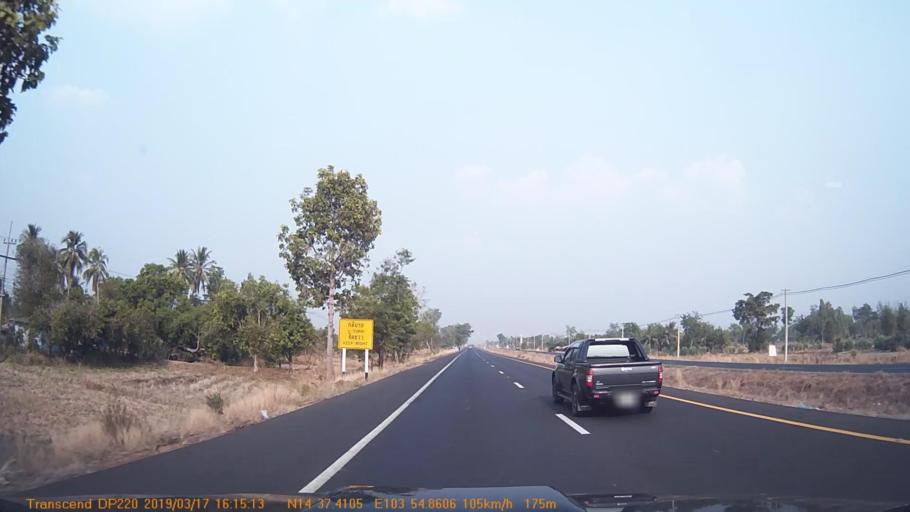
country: TH
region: Surin
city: Sangkha
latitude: 14.6235
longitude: 103.9150
